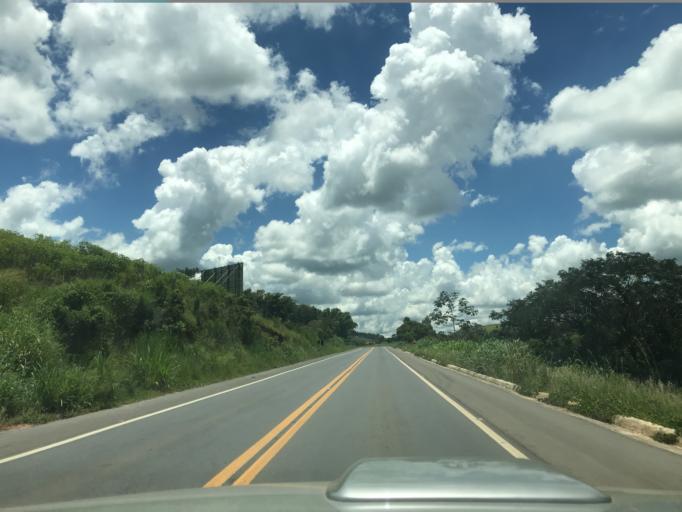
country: BR
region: Minas Gerais
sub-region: Perdoes
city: Perdoes
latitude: -21.0927
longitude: -45.1000
